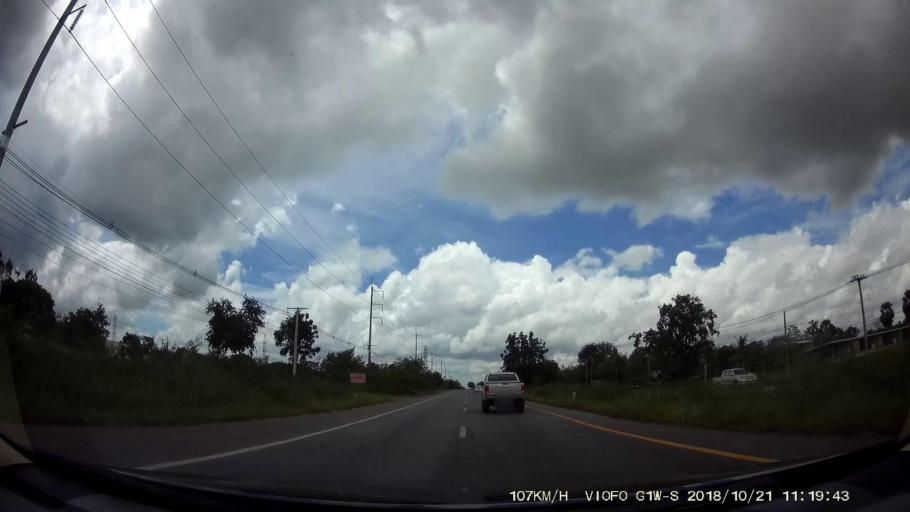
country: TH
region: Chaiyaphum
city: Chaiyaphum
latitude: 15.8649
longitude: 102.0831
